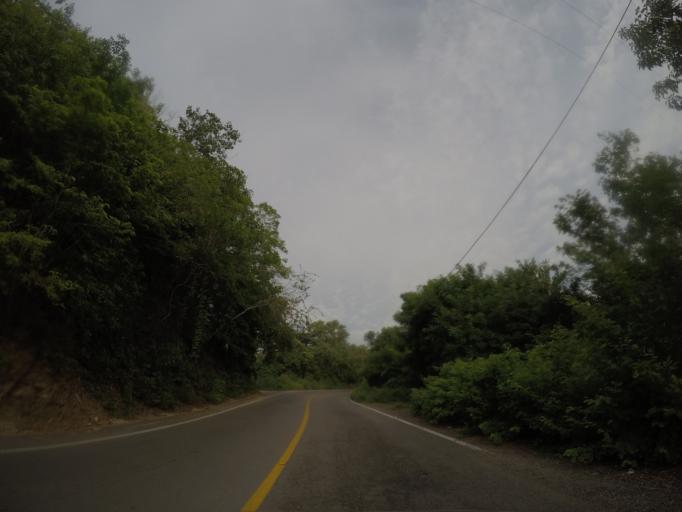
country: MX
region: Oaxaca
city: San Pedro Pochutla
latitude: 15.7059
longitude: -96.4817
